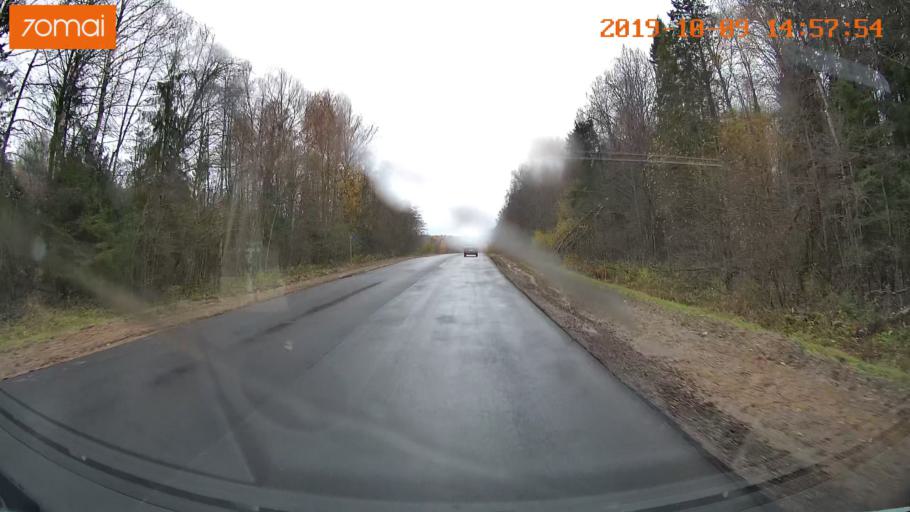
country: RU
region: Kostroma
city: Chistyye Bory
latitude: 58.3326
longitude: 41.6530
